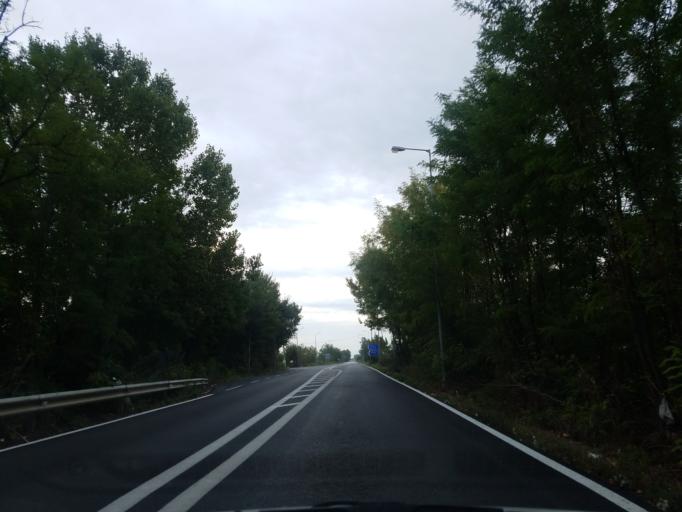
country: GR
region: Thessaly
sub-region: Nomos Kardhitsas
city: Agnantero
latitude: 39.4588
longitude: 21.8559
